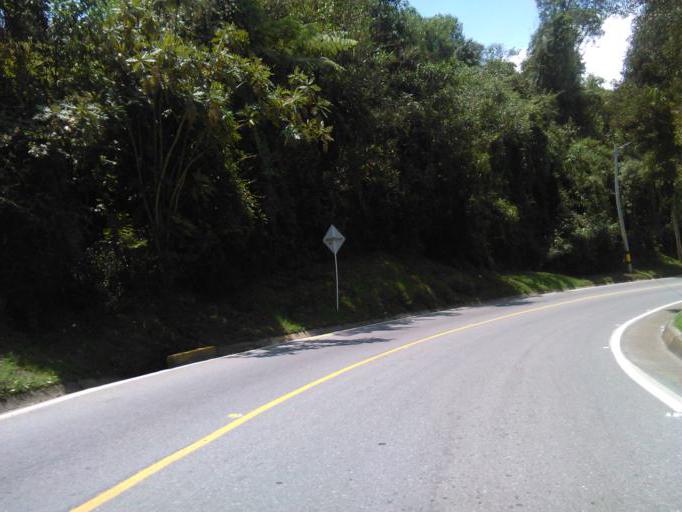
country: CO
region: Antioquia
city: La Union
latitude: 6.0012
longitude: -75.3820
